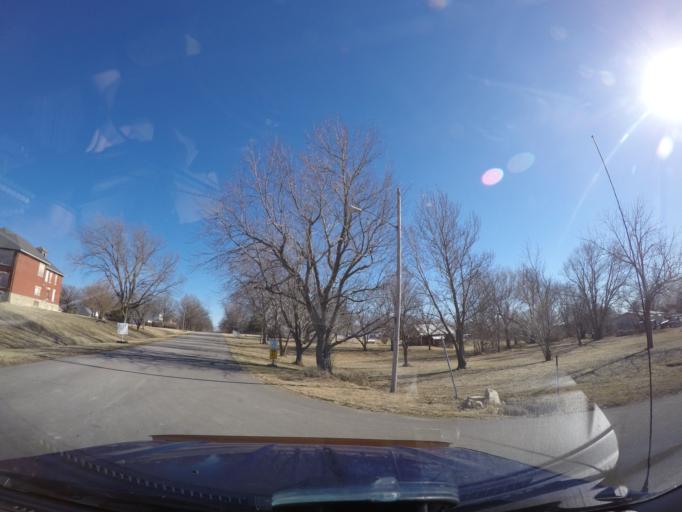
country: US
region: Kansas
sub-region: Dickinson County
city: Herington
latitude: 38.7959
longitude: -96.9642
